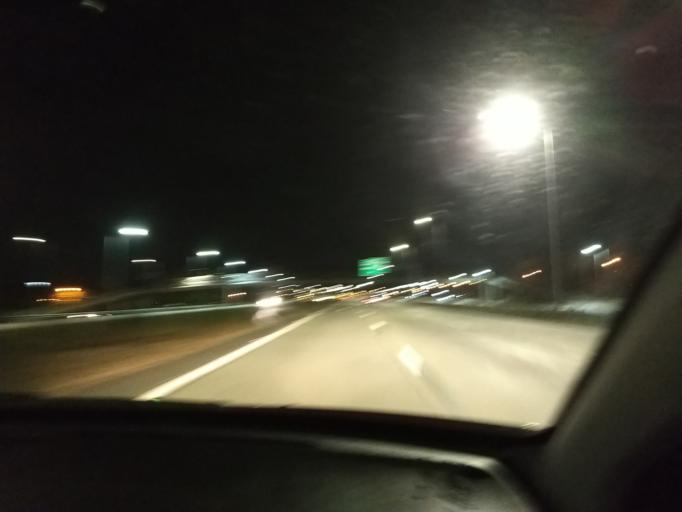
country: AR
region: Cordoba
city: La Calera
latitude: -31.3851
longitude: -64.2614
